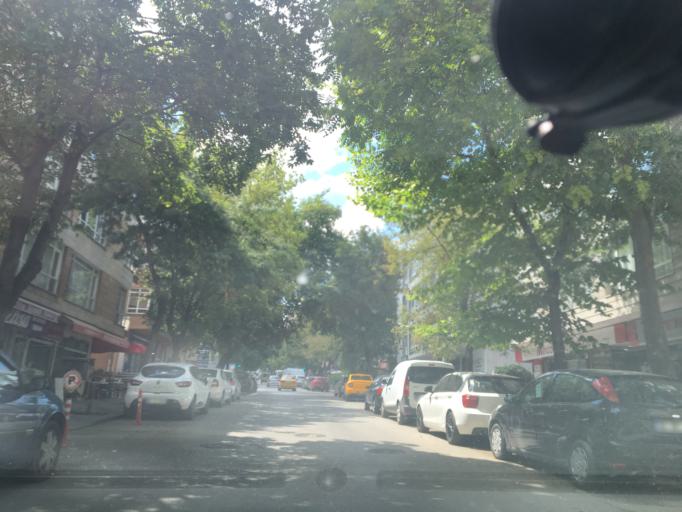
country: TR
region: Ankara
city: Ankara
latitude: 39.9032
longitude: 32.8528
